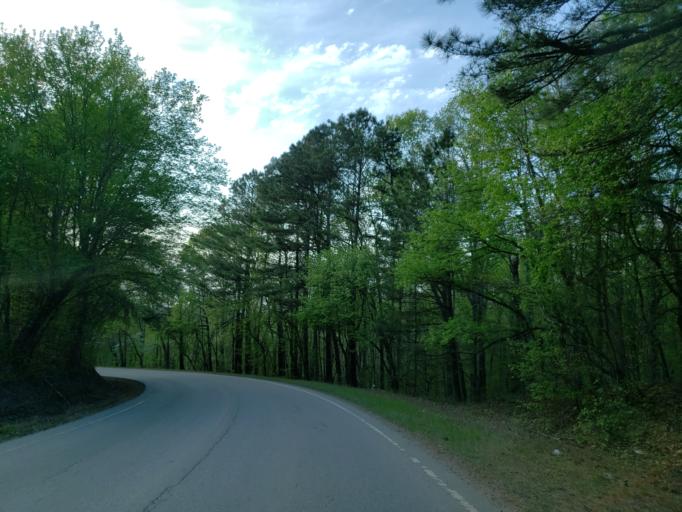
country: US
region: Georgia
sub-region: Cherokee County
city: Ball Ground
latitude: 34.2935
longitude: -84.3912
